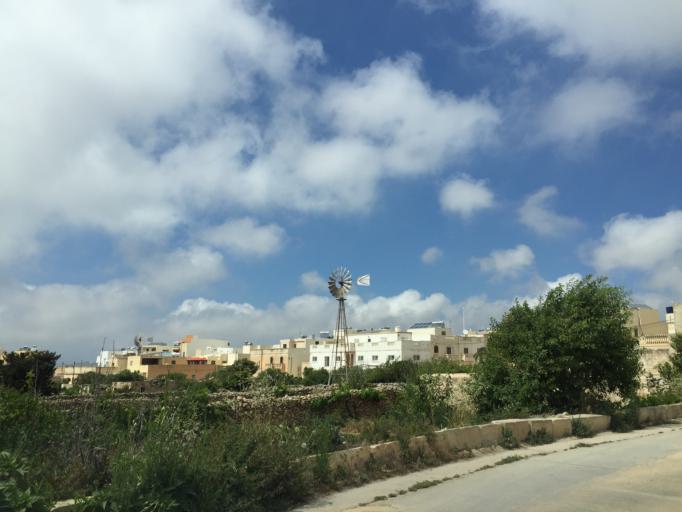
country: MT
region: Dingli
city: Dingli
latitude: 35.8585
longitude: 14.3786
